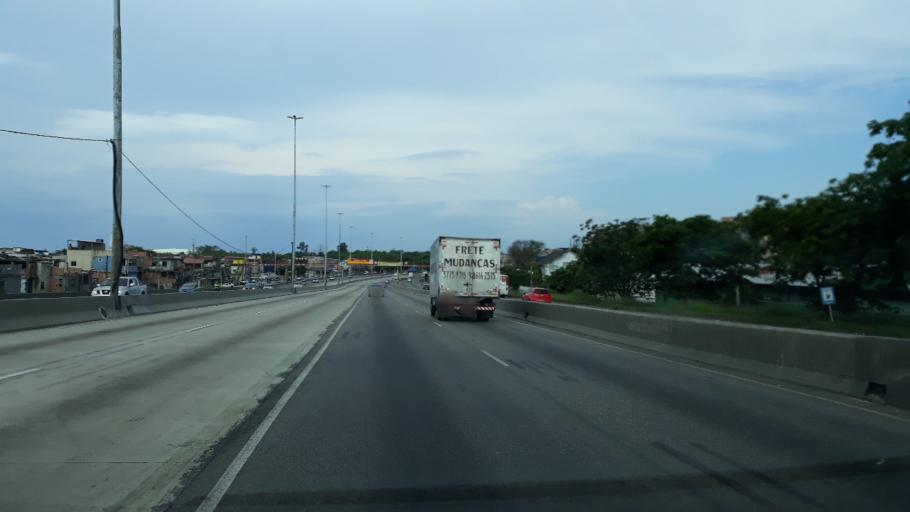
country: BR
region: Rio de Janeiro
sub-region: Duque De Caxias
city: Duque de Caxias
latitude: -22.8151
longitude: -43.2985
